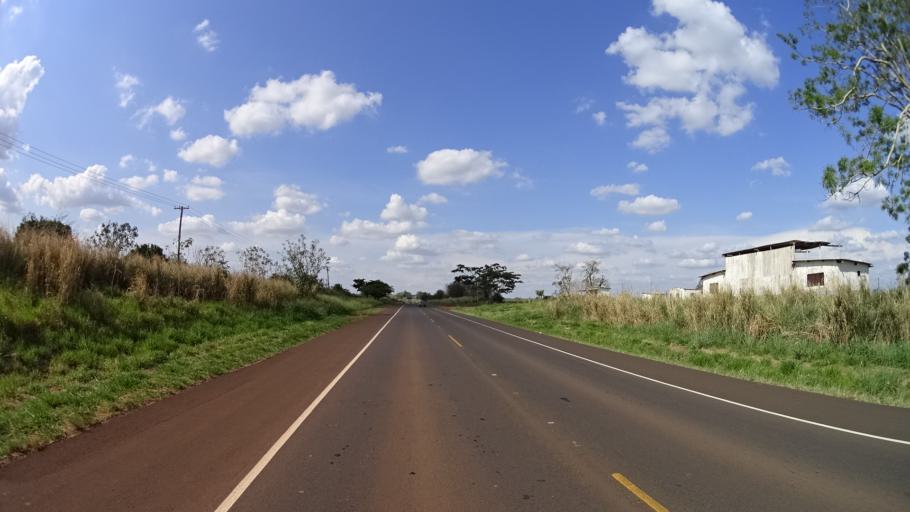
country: BR
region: Sao Paulo
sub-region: Urupes
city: Urupes
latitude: -21.0218
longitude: -49.2324
